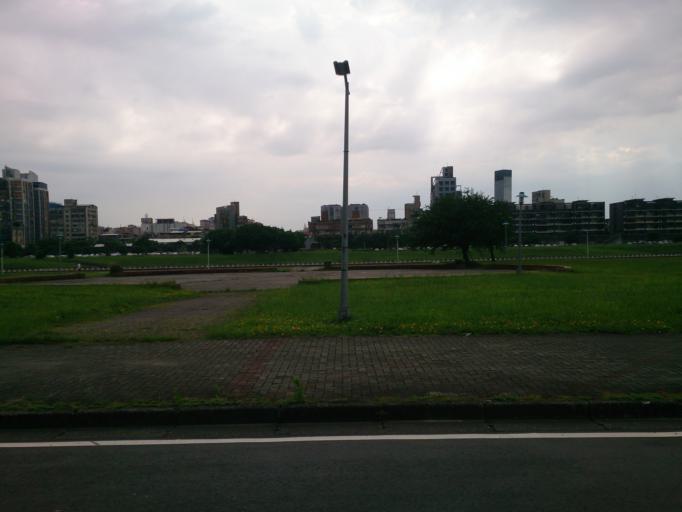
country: TW
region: Taipei
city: Taipei
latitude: 25.0596
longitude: 121.5727
